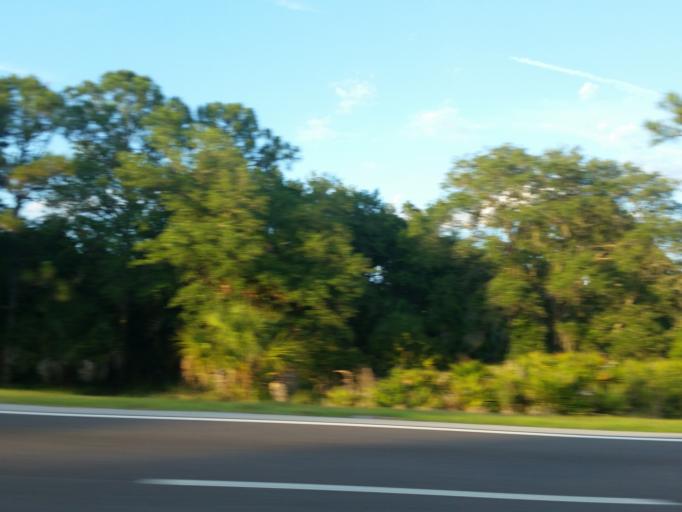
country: US
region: Florida
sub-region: Sarasota County
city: Nokomis
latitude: 27.1481
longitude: -82.4159
